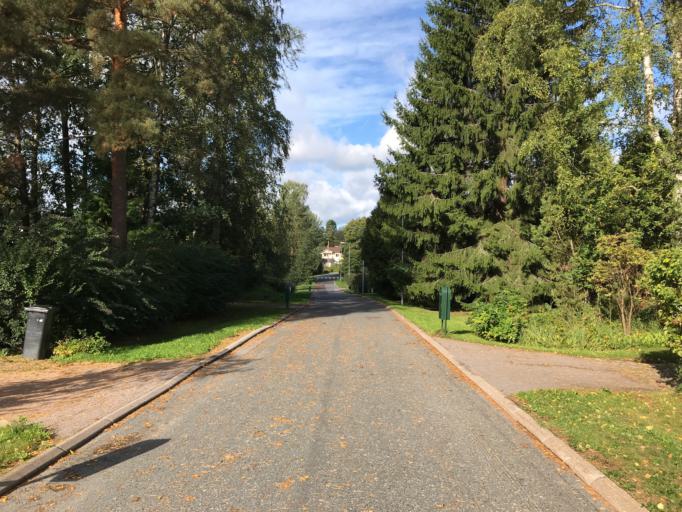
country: FI
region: Uusimaa
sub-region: Helsinki
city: Vantaa
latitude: 60.2226
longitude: 25.0564
